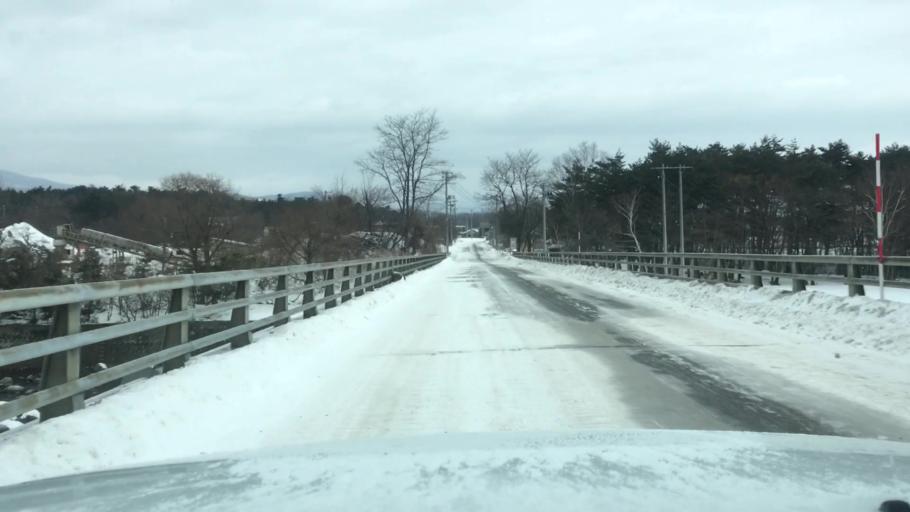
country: JP
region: Iwate
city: Shizukuishi
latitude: 39.9120
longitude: 141.0049
